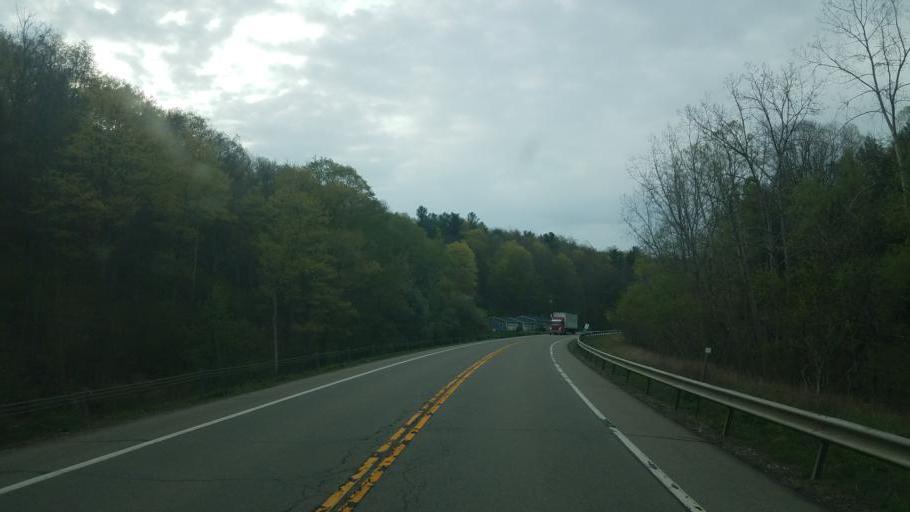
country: US
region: New York
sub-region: Steuben County
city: Canisteo
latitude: 42.1890
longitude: -77.5421
